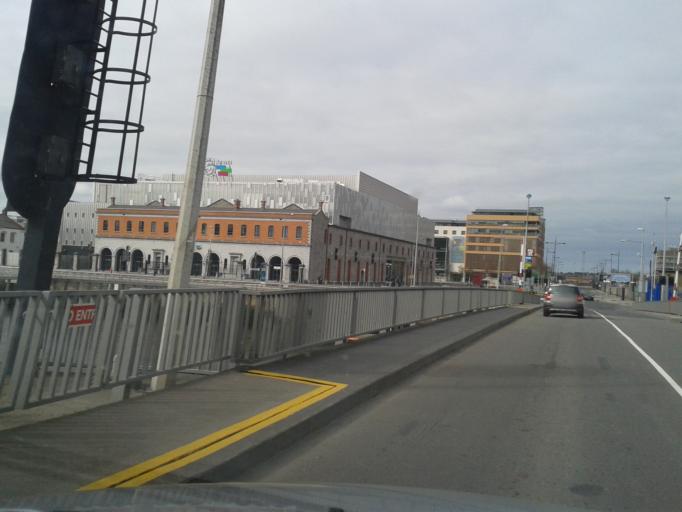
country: IE
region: Leinster
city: Ringsend
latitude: 53.3457
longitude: -6.2275
